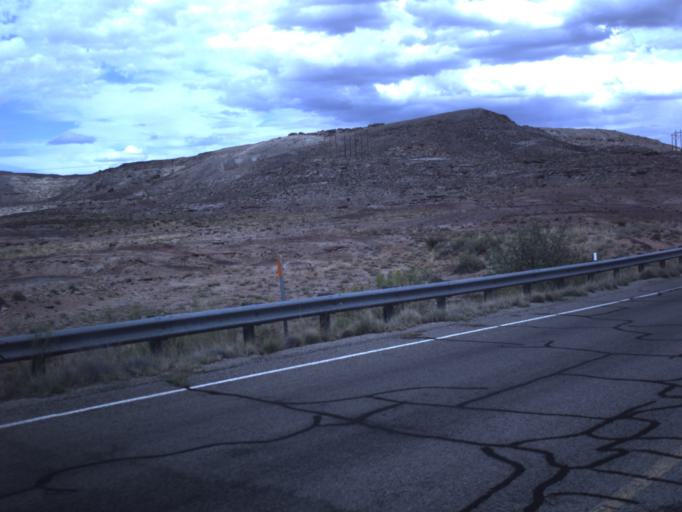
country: US
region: Utah
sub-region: San Juan County
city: Blanding
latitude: 37.2743
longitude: -109.3543
